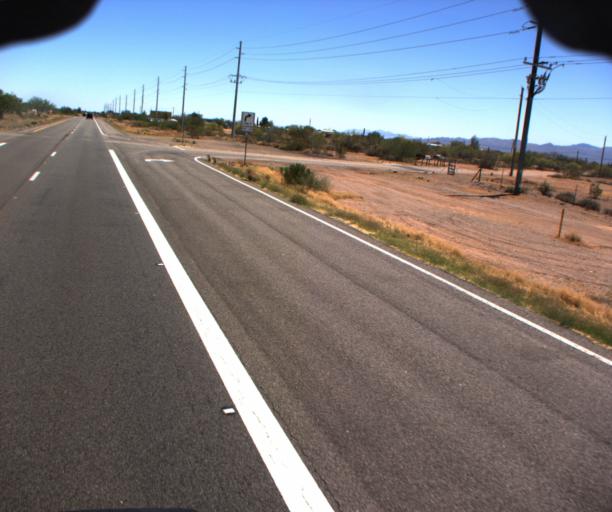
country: US
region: Arizona
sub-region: Maricopa County
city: Wickenburg
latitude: 33.8347
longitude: -112.6035
